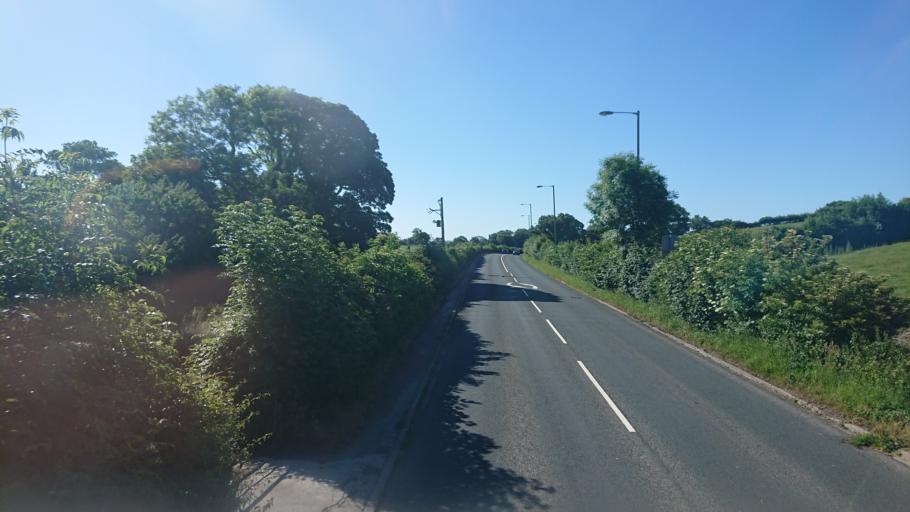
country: GB
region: England
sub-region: Lancashire
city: Galgate
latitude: 53.9859
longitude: -2.7885
